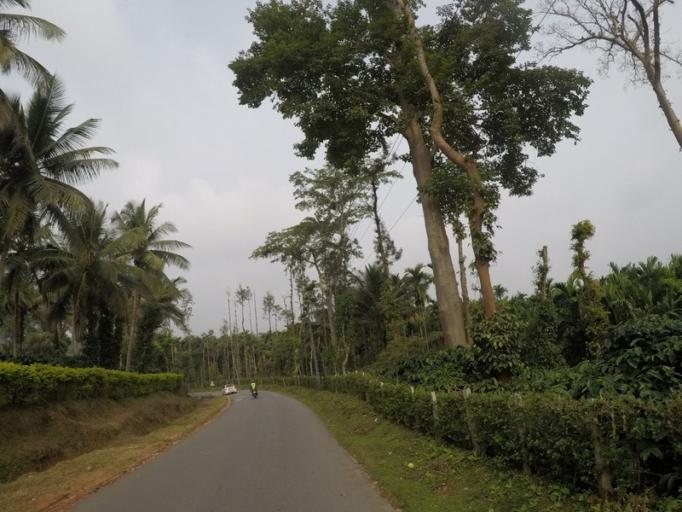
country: IN
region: Karnataka
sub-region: Chikmagalur
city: Chikmagalur
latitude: 13.3525
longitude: 75.5400
